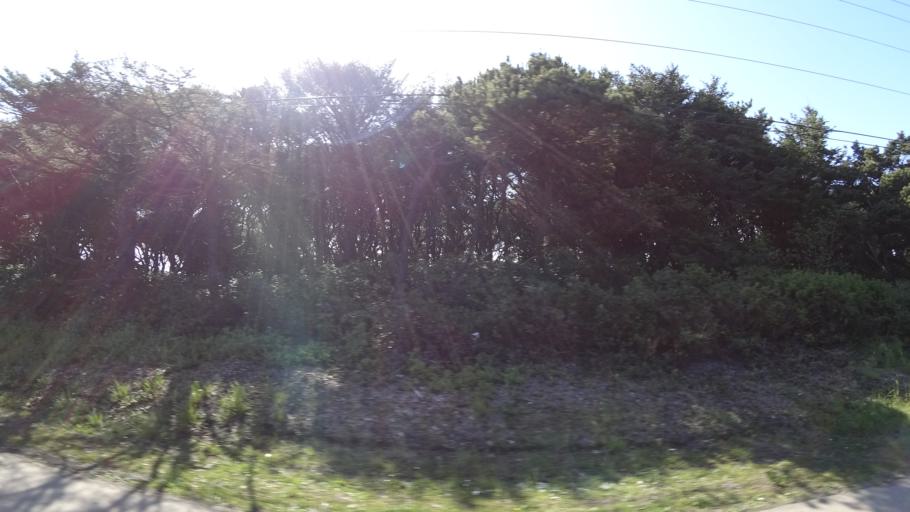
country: US
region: Oregon
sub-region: Lincoln County
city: Newport
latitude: 44.5525
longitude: -124.0721
